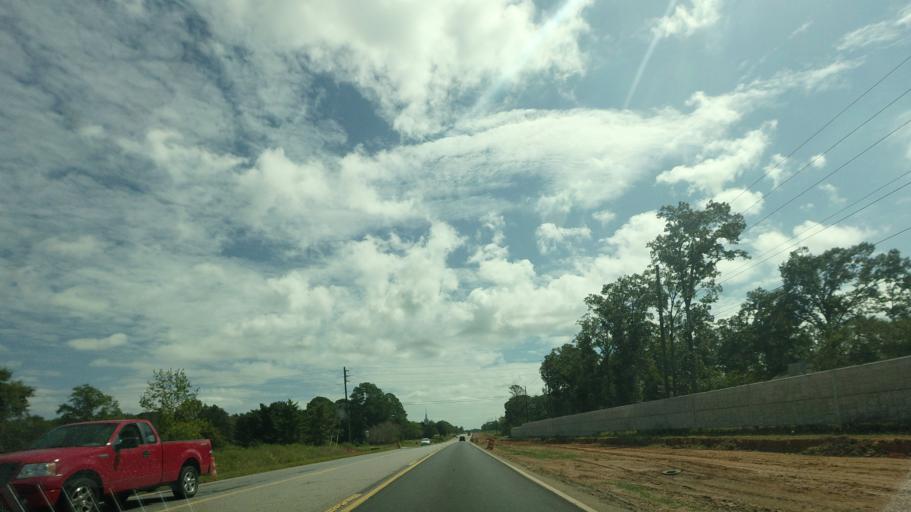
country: US
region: Georgia
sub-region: Houston County
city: Warner Robins
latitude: 32.5545
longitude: -83.6419
